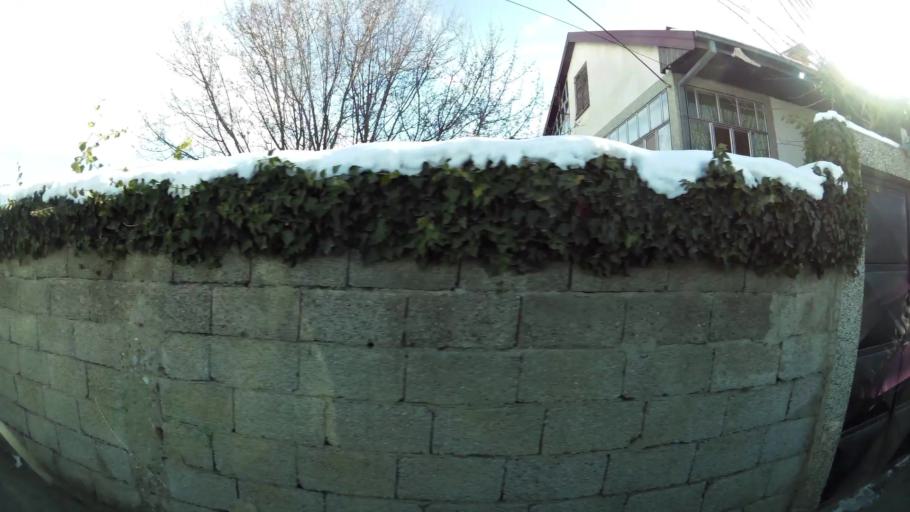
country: MK
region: Saraj
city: Saraj
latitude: 41.9980
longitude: 21.3186
